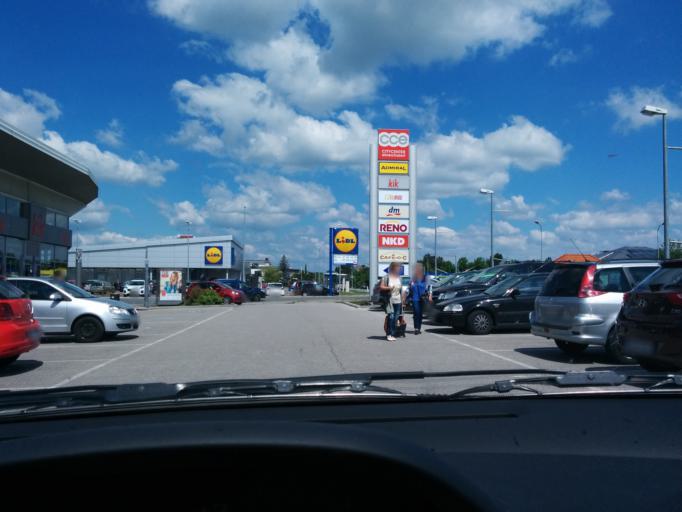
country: AT
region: Lower Austria
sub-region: Politischer Bezirk Baden
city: Ebreichsdorf
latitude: 47.9553
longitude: 16.4030
